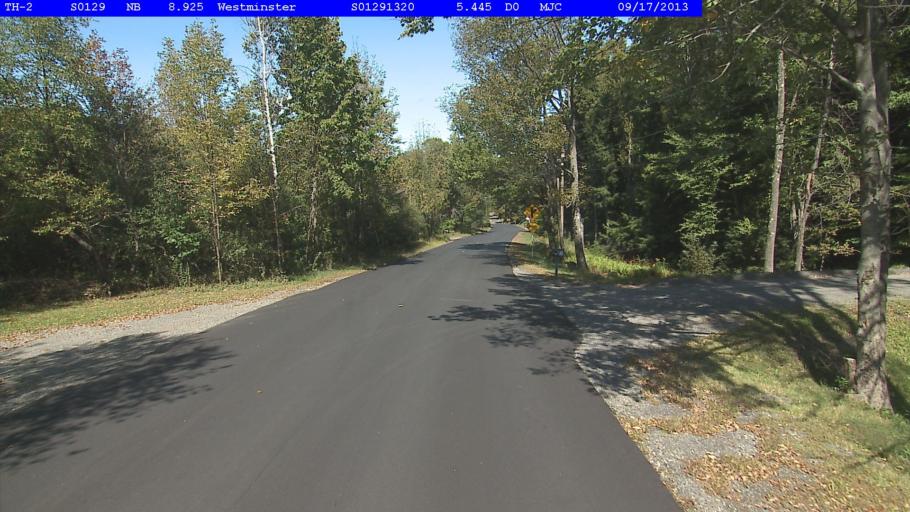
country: US
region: Vermont
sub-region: Windham County
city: Bellows Falls
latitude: 43.0934
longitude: -72.5355
